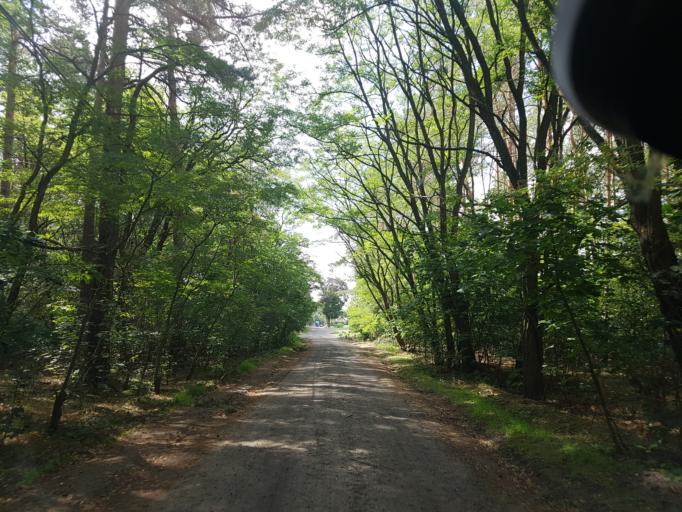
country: DE
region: Brandenburg
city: Fichtenwalde
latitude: 52.2917
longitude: 12.8598
